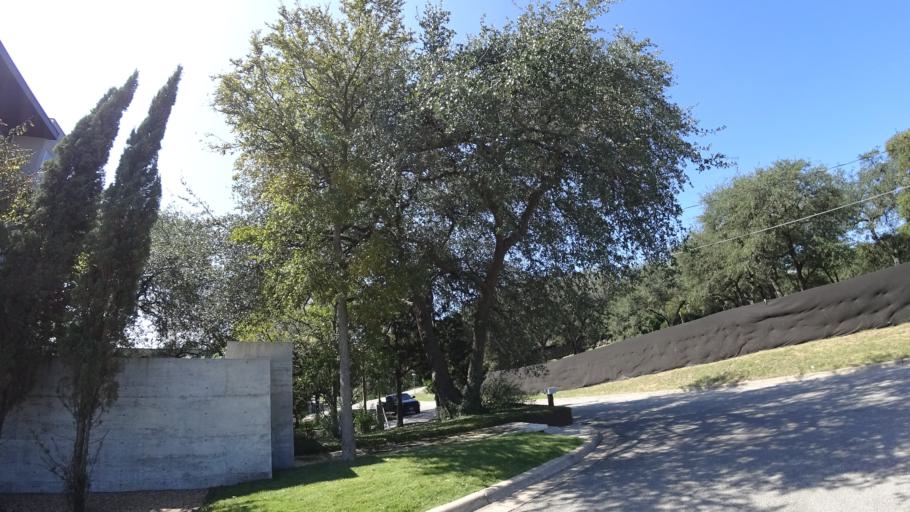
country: US
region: Texas
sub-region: Travis County
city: West Lake Hills
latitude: 30.3036
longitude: -97.7855
